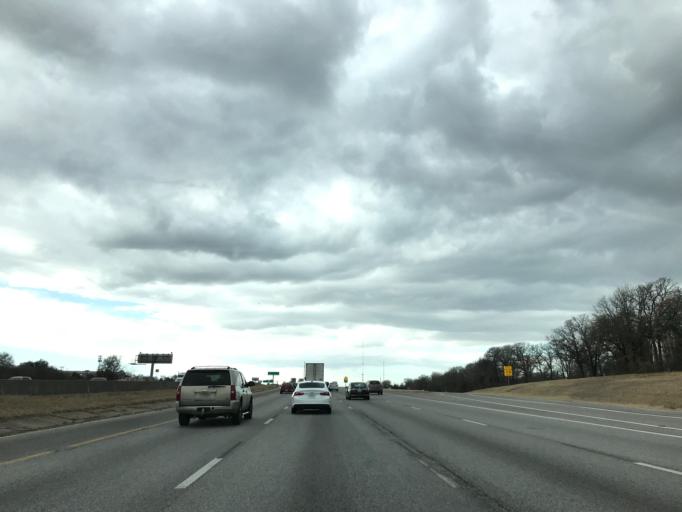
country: US
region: Texas
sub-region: Tarrant County
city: Dalworthington Gardens
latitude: 32.6763
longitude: -97.1878
